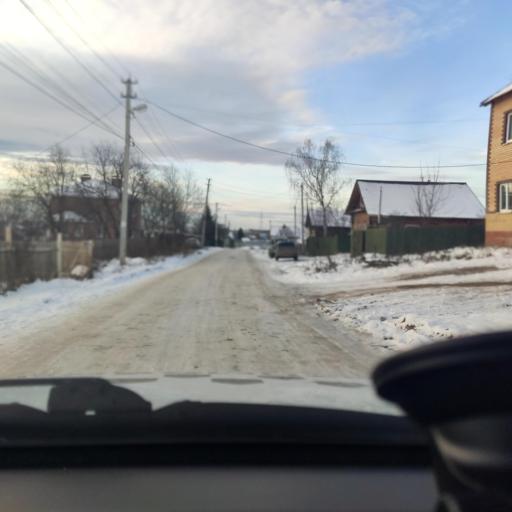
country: RU
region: Perm
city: Ferma
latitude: 57.9416
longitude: 56.3512
